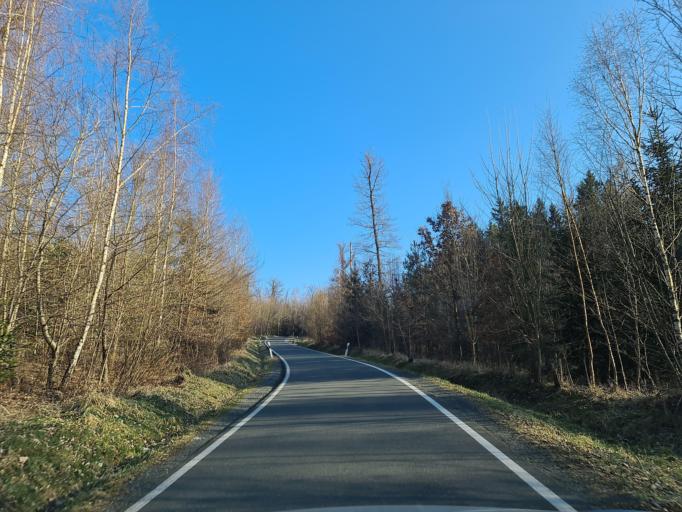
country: DE
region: Saxony
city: Pohl
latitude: 50.5371
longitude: 12.1574
